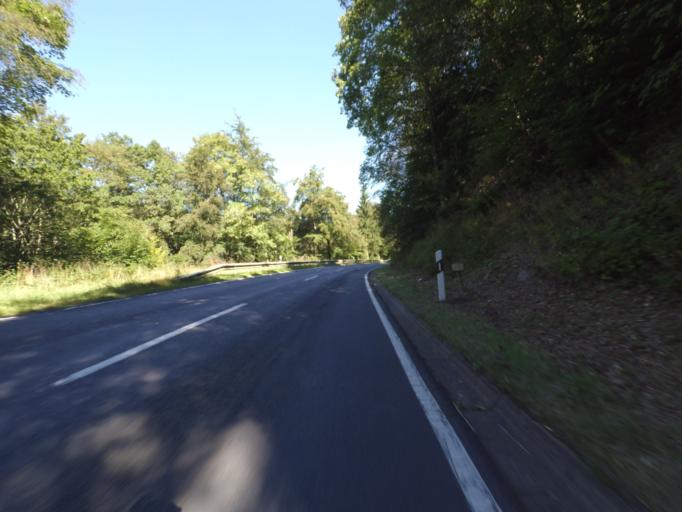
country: DE
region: Rheinland-Pfalz
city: Mullenbach
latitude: 50.1981
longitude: 7.0587
